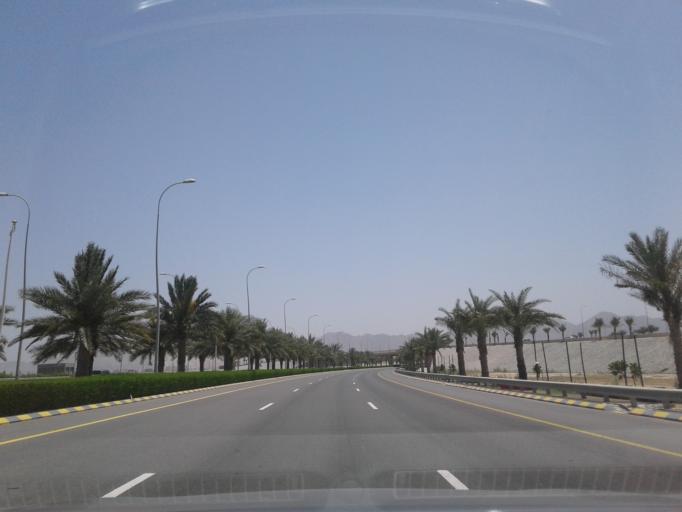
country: OM
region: Muhafazat Masqat
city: Bawshar
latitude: 23.6005
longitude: 58.3265
